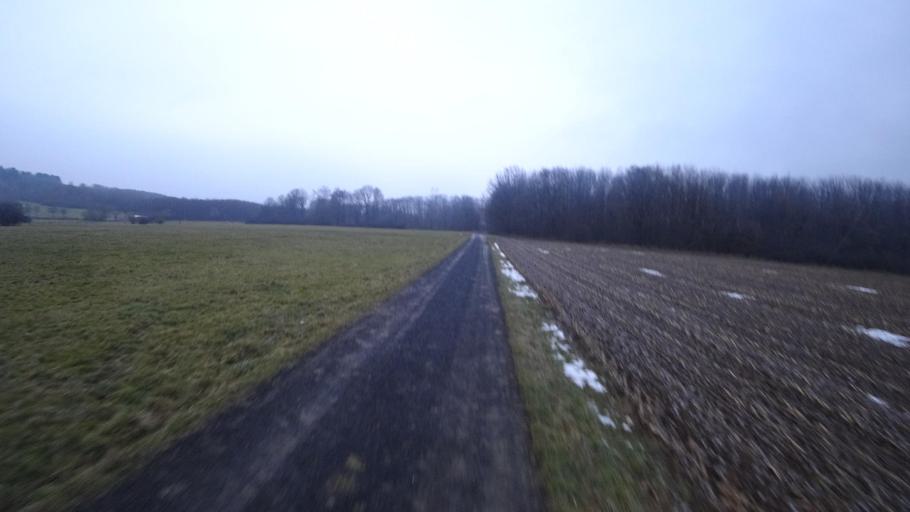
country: DE
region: Rheinland-Pfalz
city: Ailertchen
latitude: 50.6060
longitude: 7.9202
